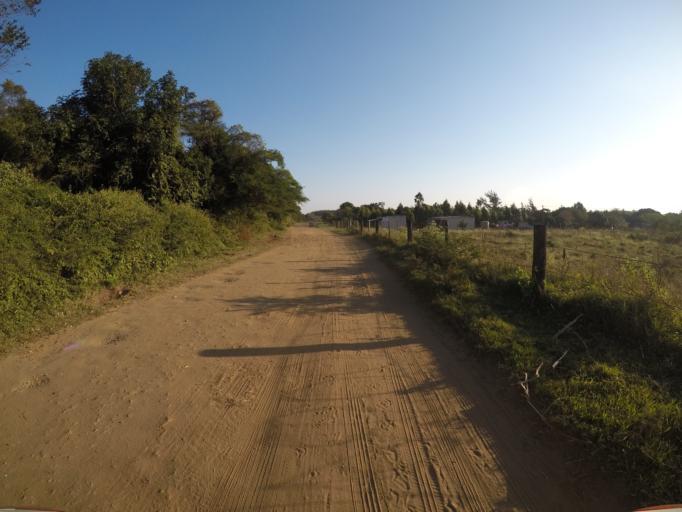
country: ZA
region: KwaZulu-Natal
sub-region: uThungulu District Municipality
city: KwaMbonambi
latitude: -28.7051
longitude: 32.1874
